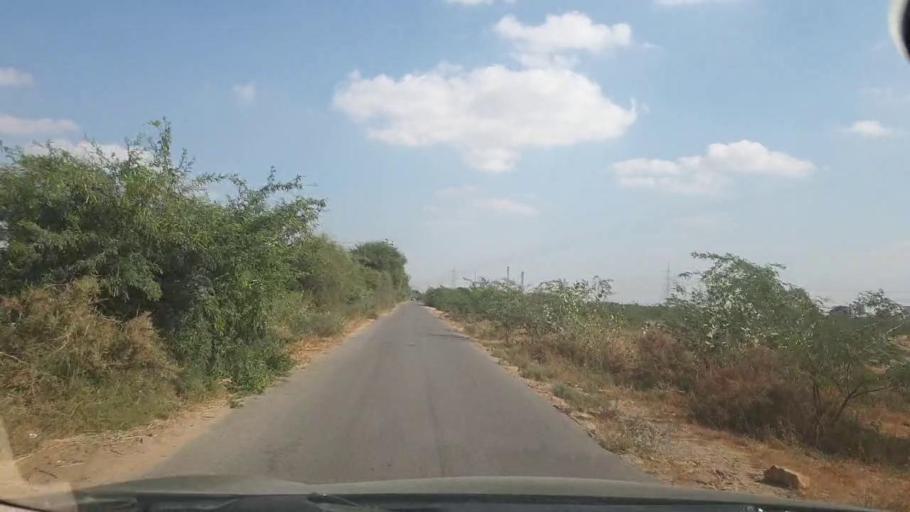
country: PK
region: Sindh
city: Malir Cantonment
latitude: 25.0177
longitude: 67.3576
